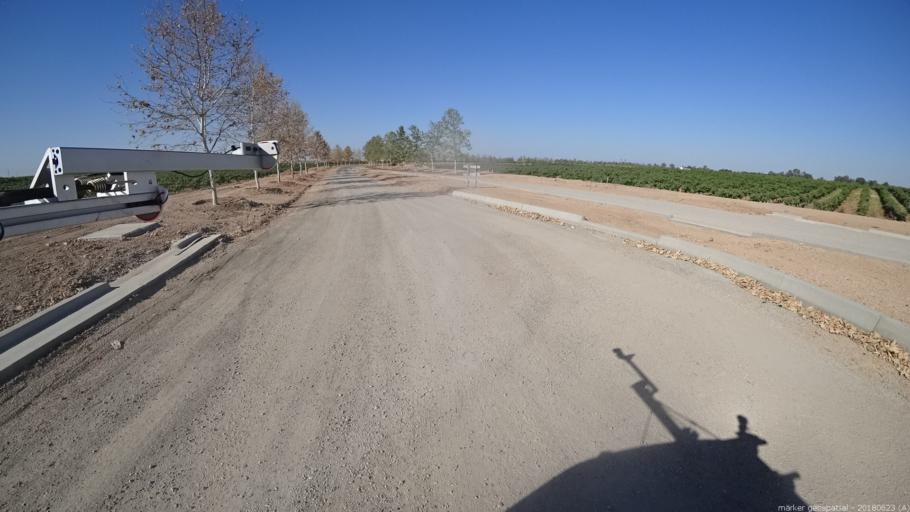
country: US
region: California
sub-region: Madera County
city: Bonadelle Ranchos-Madera Ranchos
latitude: 36.9623
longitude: -119.7857
